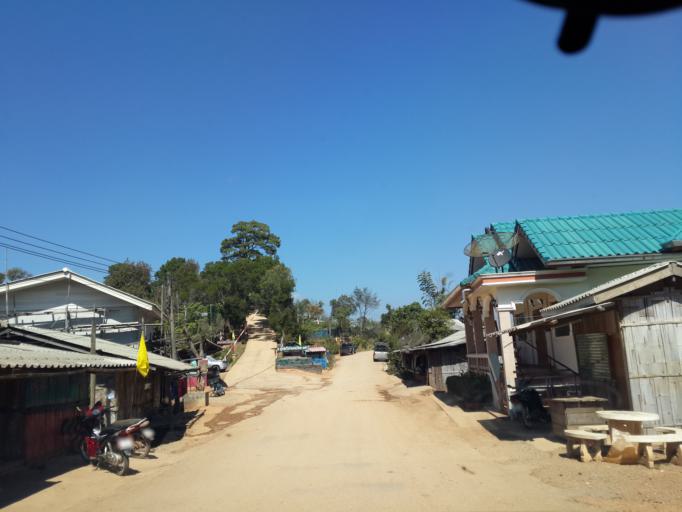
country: TH
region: Chiang Mai
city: Fang
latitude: 19.9381
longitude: 99.0415
